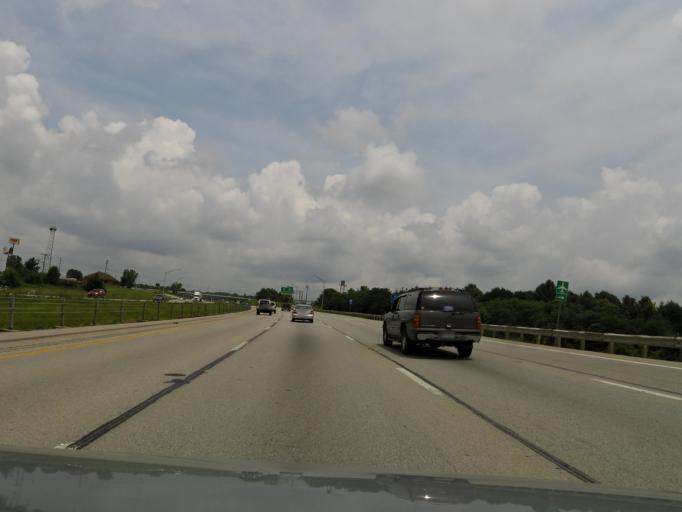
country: US
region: Kentucky
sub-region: Hardin County
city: Elizabethtown
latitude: 37.7086
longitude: -85.8300
